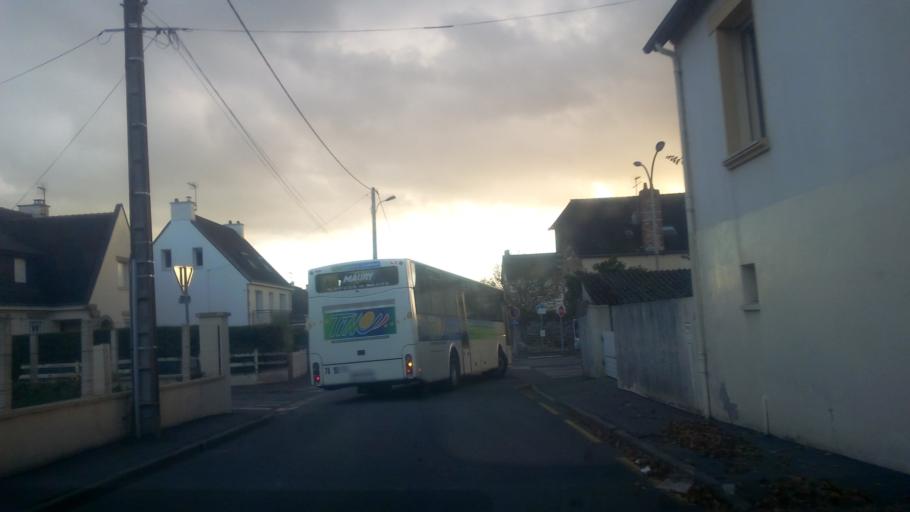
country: FR
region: Brittany
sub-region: Departement d'Ille-et-Vilaine
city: Redon
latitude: 47.6493
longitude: -2.0944
